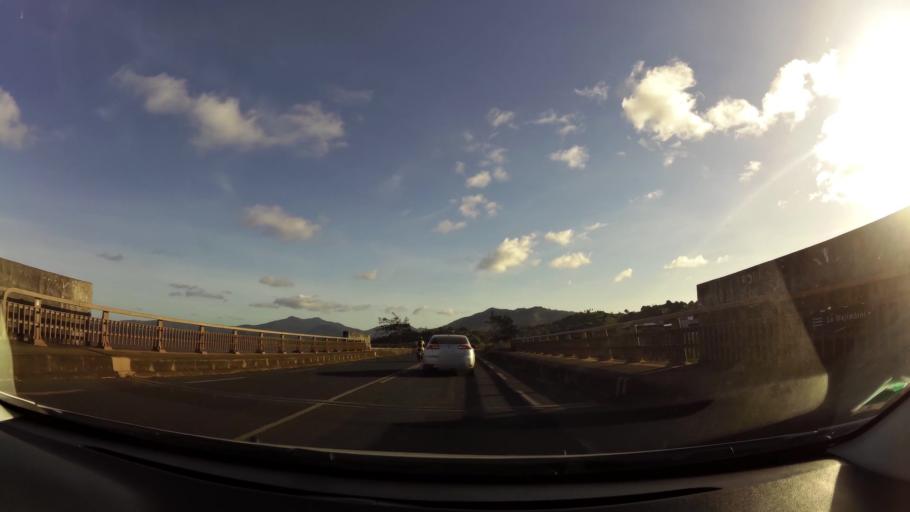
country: YT
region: Mamoudzou
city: Mamoudzou
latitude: -12.7911
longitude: 45.2231
